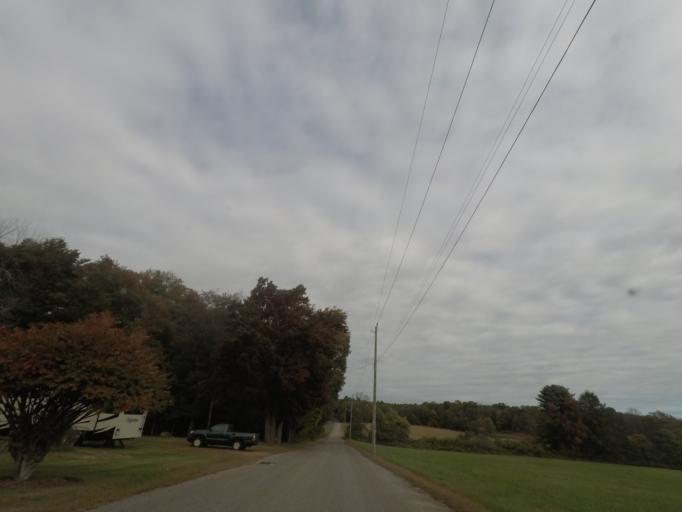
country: US
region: Connecticut
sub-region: Windham County
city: Thompson
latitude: 41.9584
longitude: -71.8337
